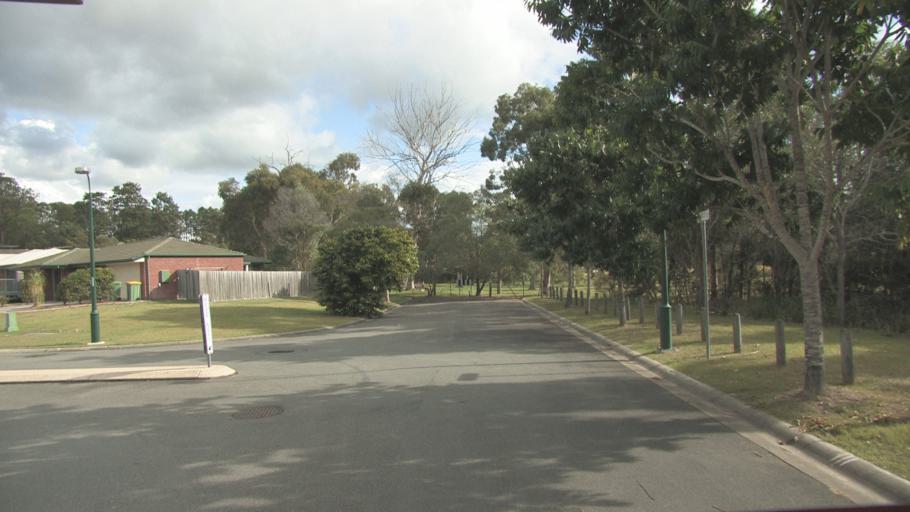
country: AU
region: Queensland
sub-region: Logan
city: Logan Reserve
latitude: -27.6923
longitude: 153.0924
